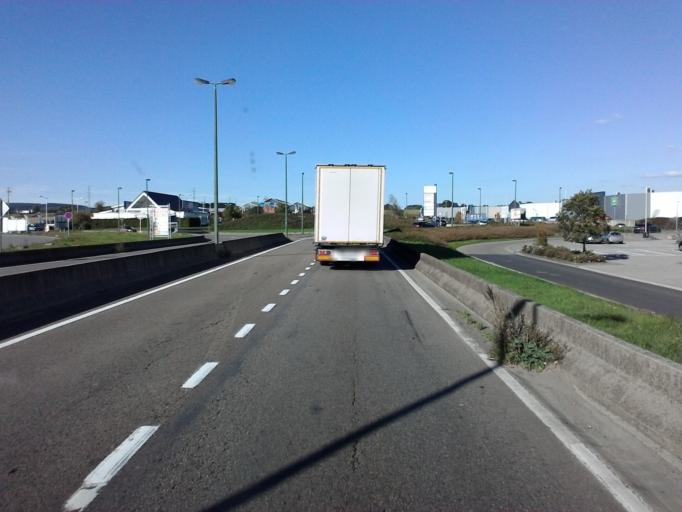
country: BE
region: Wallonia
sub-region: Province du Luxembourg
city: Messancy
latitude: 49.6235
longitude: 5.8104
